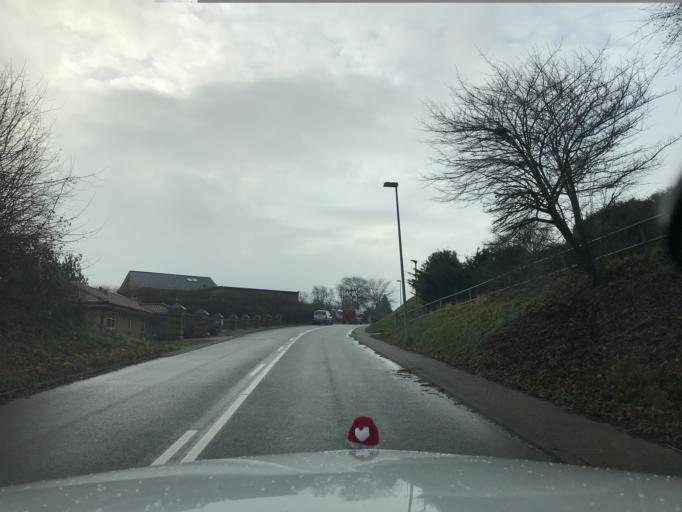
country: DK
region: South Denmark
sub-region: Sonderborg Kommune
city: Grasten
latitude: 54.8921
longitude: 9.5627
